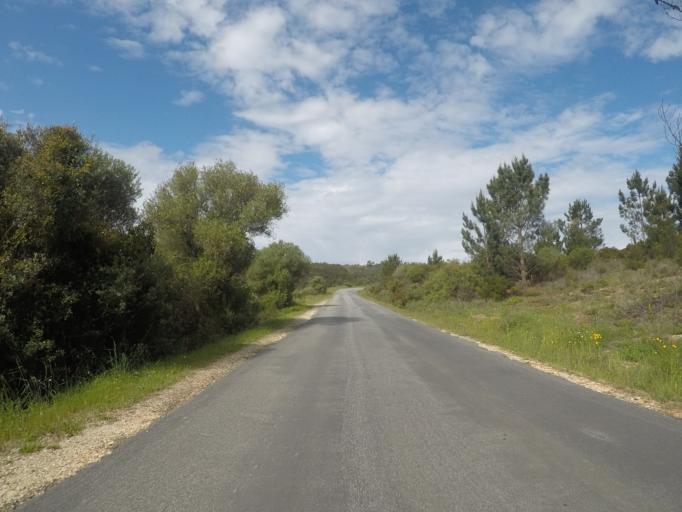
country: PT
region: Beja
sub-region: Odemira
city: Sao Teotonio
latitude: 37.4355
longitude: -8.7812
